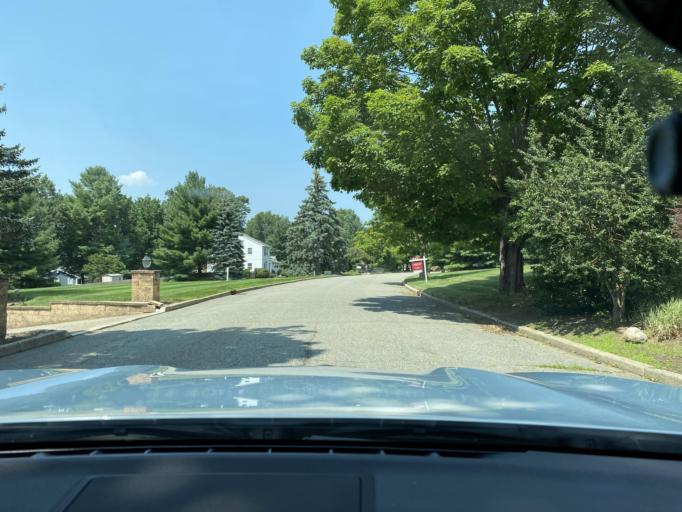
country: US
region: New York
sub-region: Rockland County
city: Airmont
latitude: 41.0912
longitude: -74.1180
